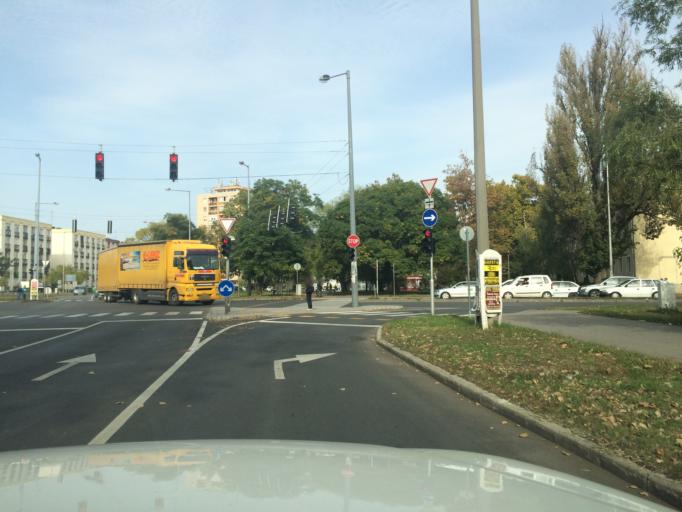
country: HU
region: Szabolcs-Szatmar-Bereg
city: Nyiregyhaza
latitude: 47.9652
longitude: 21.7110
